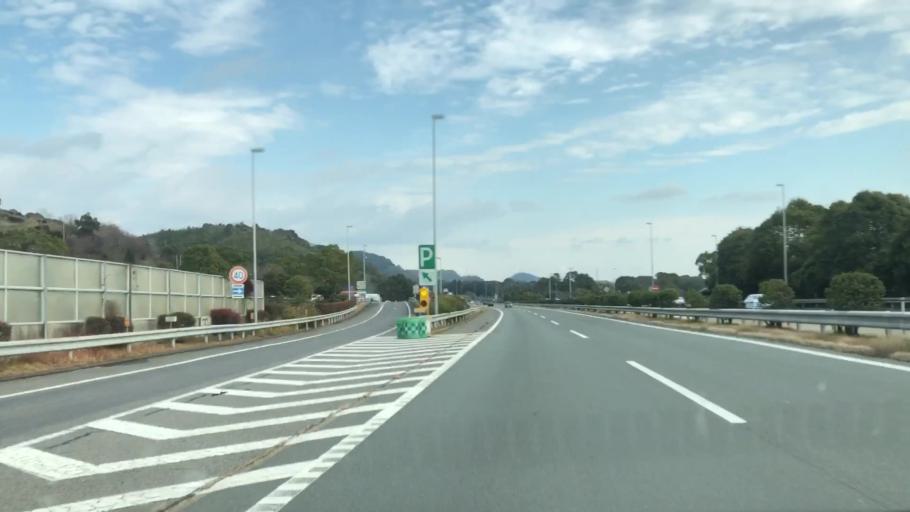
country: JP
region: Saga Prefecture
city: Kanzakimachi-kanzaki
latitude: 33.3287
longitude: 130.3089
